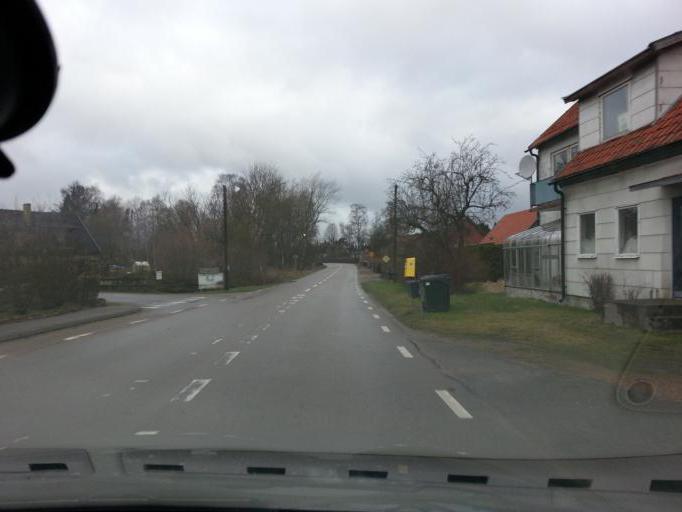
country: SE
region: Skane
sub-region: Klippans Kommun
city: Klippan
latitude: 56.0946
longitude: 13.1459
